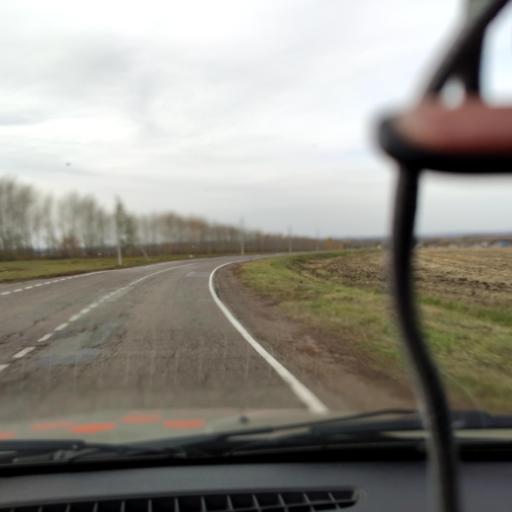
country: RU
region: Bashkortostan
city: Kabakovo
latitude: 54.5195
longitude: 56.0392
